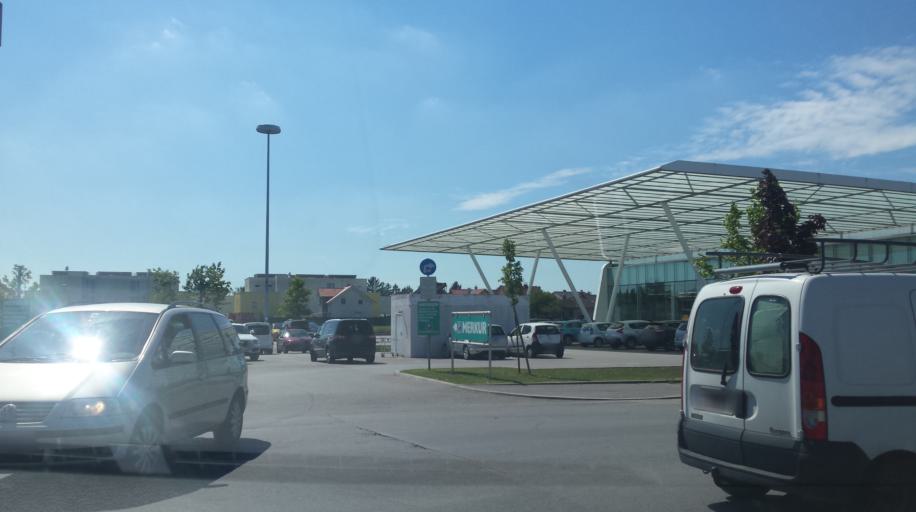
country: AT
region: Lower Austria
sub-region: Politischer Bezirk Ganserndorf
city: Deutsch-Wagram
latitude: 48.3037
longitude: 16.5757
